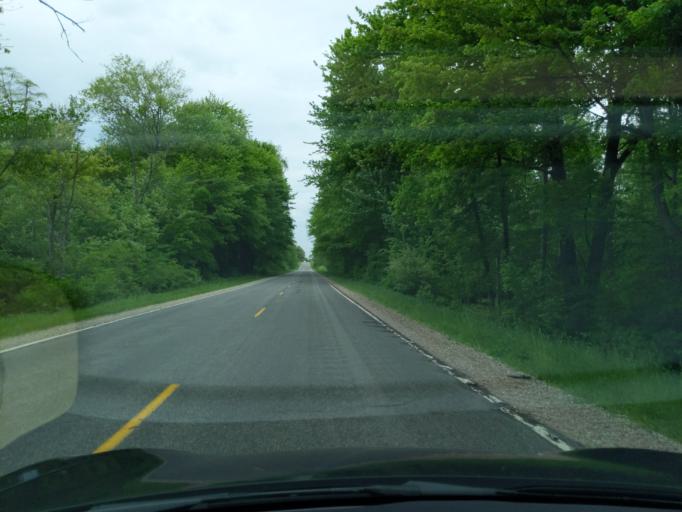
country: US
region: Michigan
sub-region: Ingham County
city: Mason
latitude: 42.5334
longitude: -84.3564
